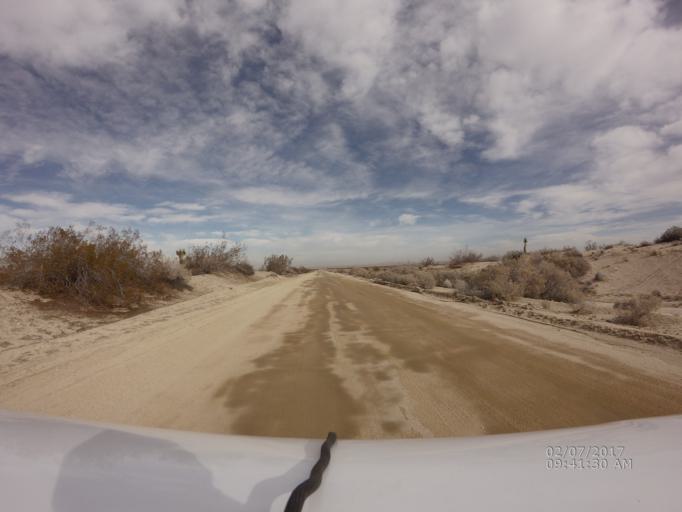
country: US
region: California
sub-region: Los Angeles County
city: Lake Los Angeles
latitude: 34.5698
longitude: -117.7114
